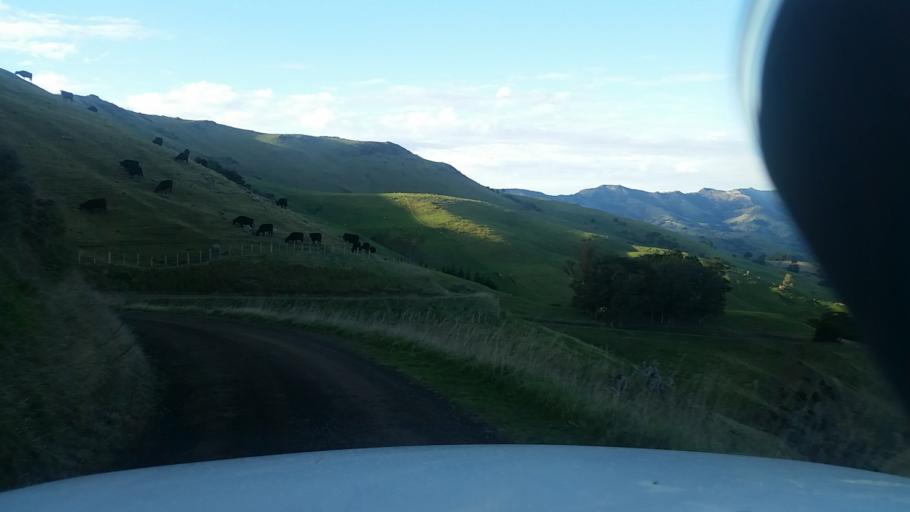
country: NZ
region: Canterbury
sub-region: Christchurch City
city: Christchurch
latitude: -43.7288
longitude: 172.9589
